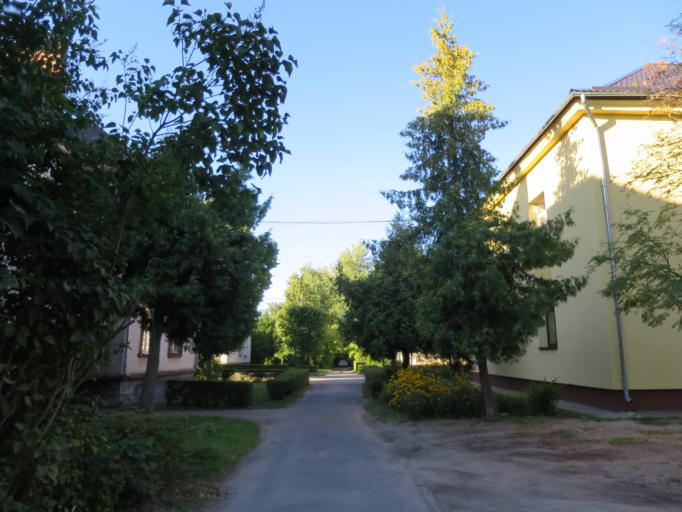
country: LV
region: Incukalns
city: Vangazi
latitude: 57.0930
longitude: 24.5459
